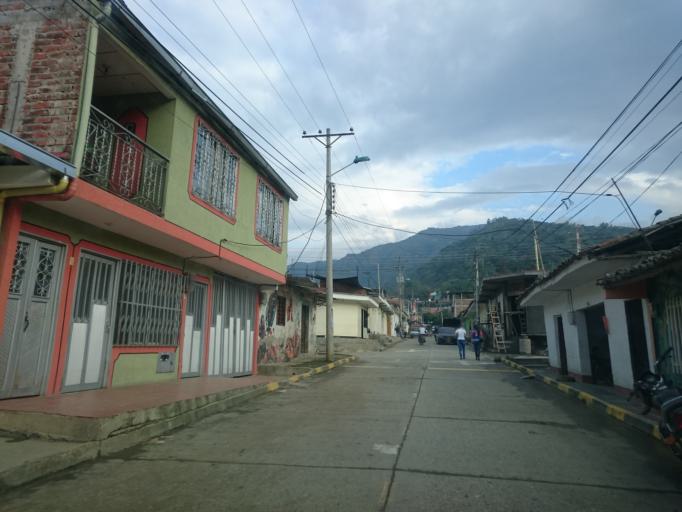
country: CO
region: Cauca
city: Toribio
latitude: 2.9569
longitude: -76.2693
